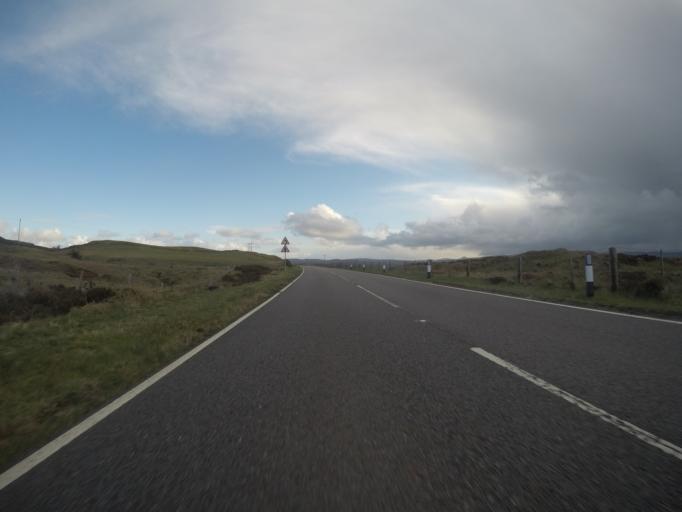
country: GB
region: Scotland
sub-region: Highland
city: Portree
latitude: 57.5546
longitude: -6.3654
